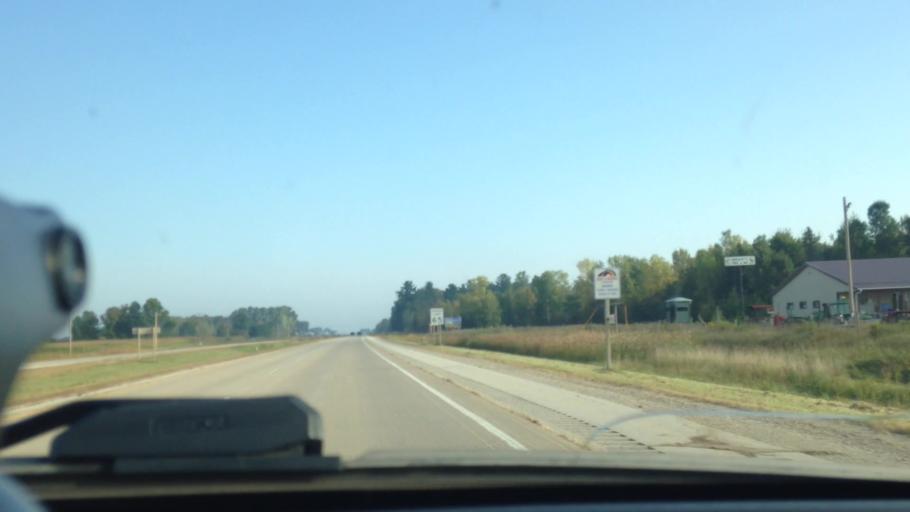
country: US
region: Wisconsin
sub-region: Oconto County
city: Oconto Falls
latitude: 45.0225
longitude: -88.0448
